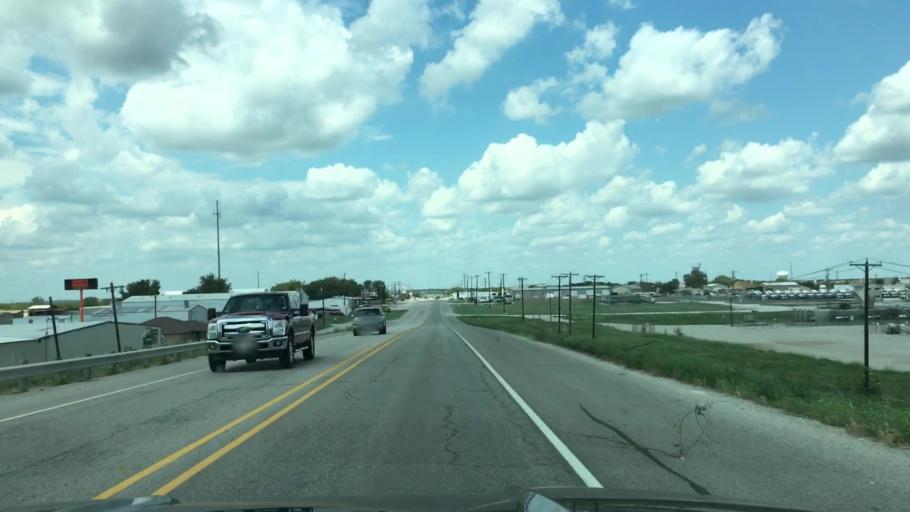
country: US
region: Texas
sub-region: Tarrant County
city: Eagle Mountain
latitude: 32.9460
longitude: -97.4208
